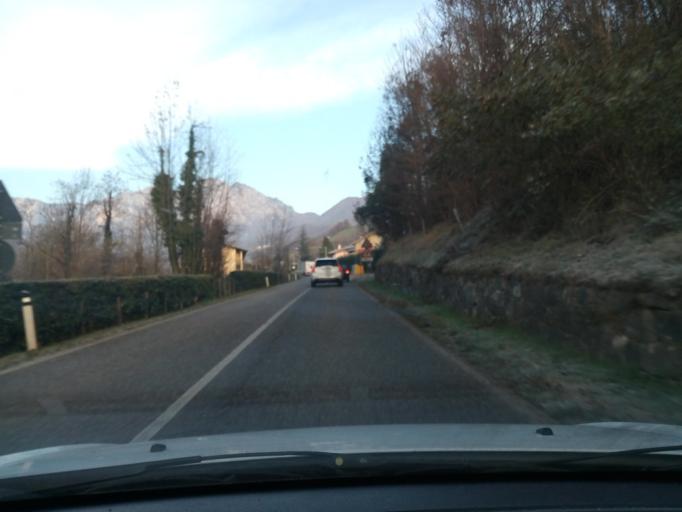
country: IT
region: Veneto
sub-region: Provincia di Vicenza
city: Valli del Pasubio
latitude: 45.7292
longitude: 11.2786
